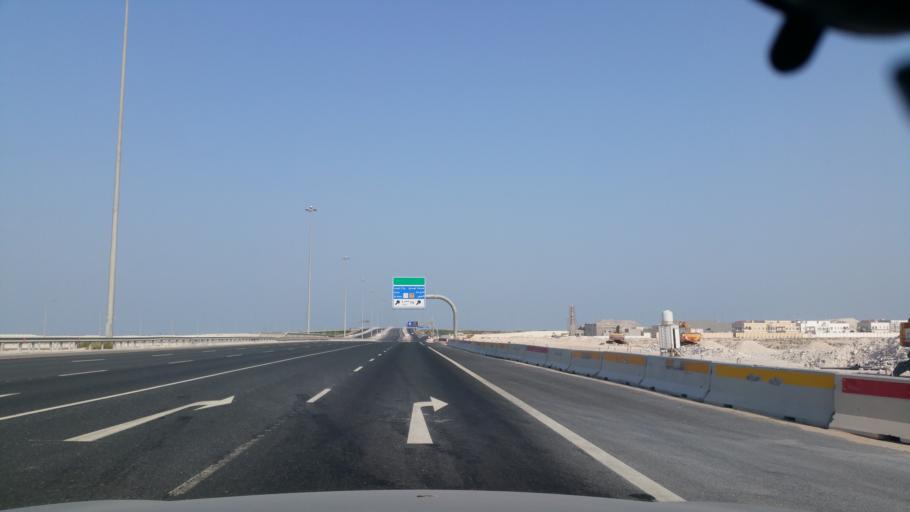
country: QA
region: Baladiyat Umm Salal
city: Umm Salal `Ali
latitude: 25.4567
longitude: 51.4680
